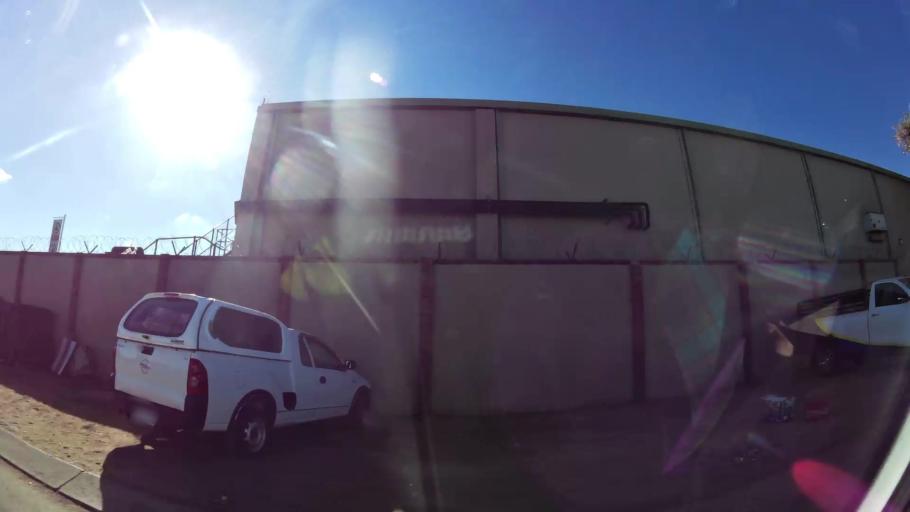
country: ZA
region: Limpopo
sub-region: Capricorn District Municipality
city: Polokwane
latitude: -23.9017
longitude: 29.4449
